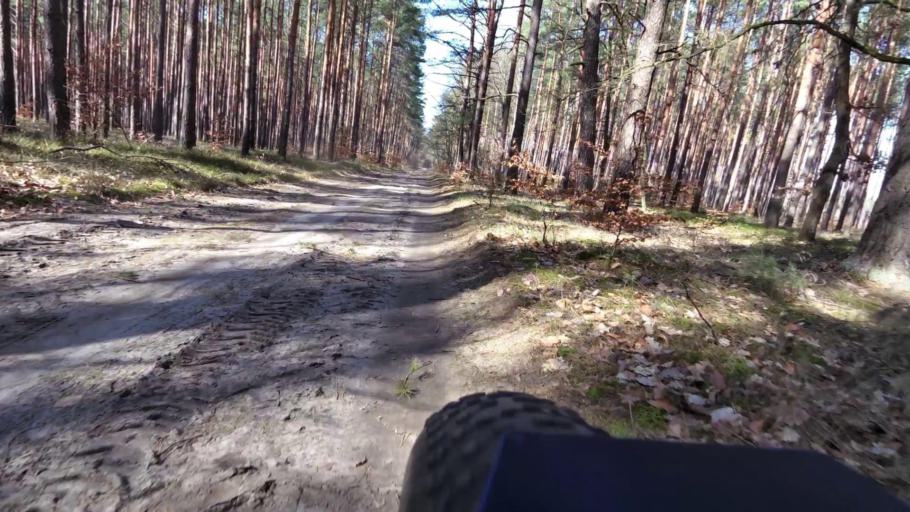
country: PL
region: Lubusz
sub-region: Powiat slubicki
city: Cybinka
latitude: 52.2033
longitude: 14.8780
